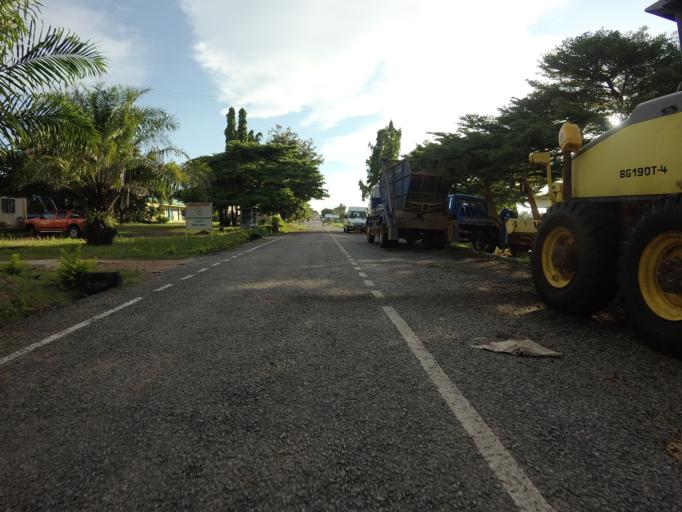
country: GH
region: Ashanti
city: Tafo
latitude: 6.9422
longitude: -1.6741
